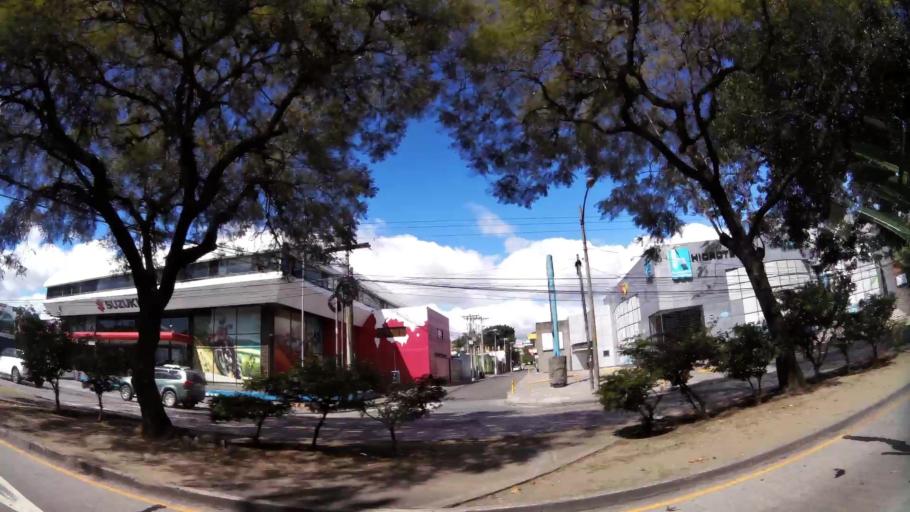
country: GT
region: Guatemala
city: Guatemala City
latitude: 14.6082
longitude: -90.5265
